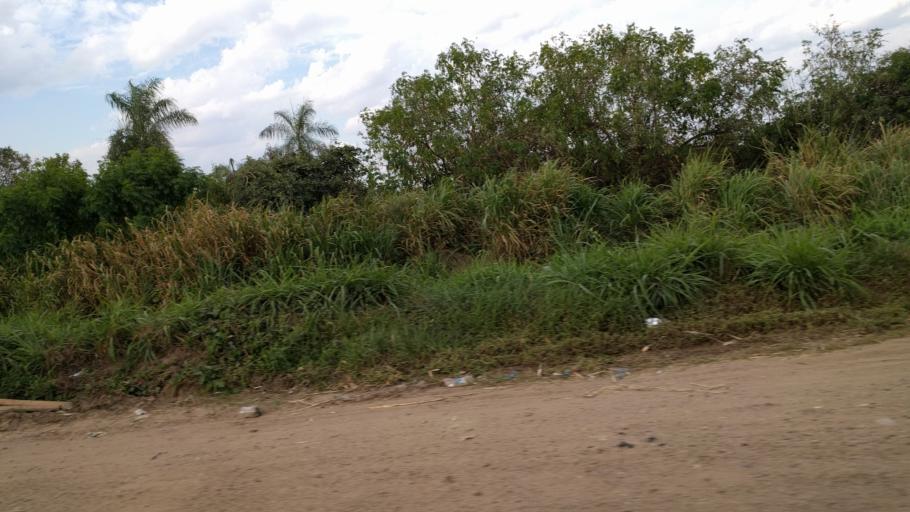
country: BO
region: Santa Cruz
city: Warnes
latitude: -17.5404
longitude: -63.1607
